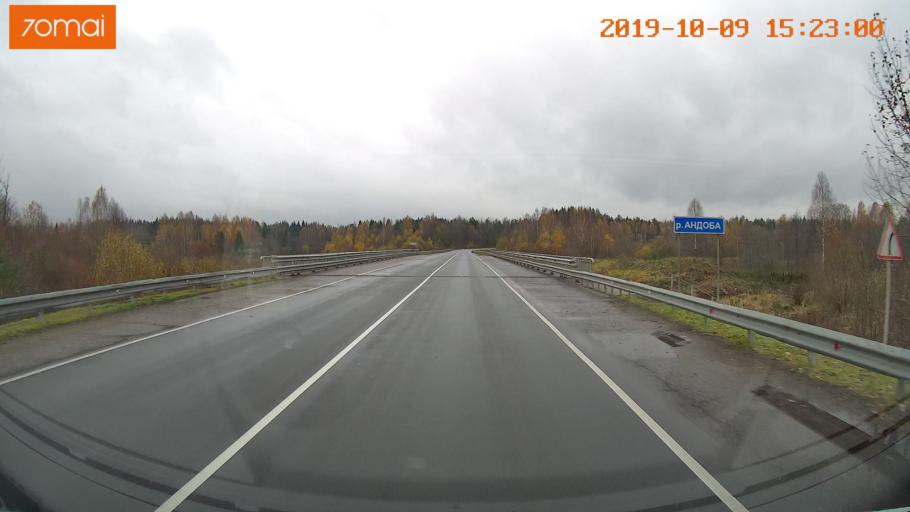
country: RU
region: Kostroma
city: Susanino
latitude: 58.0395
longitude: 41.4881
